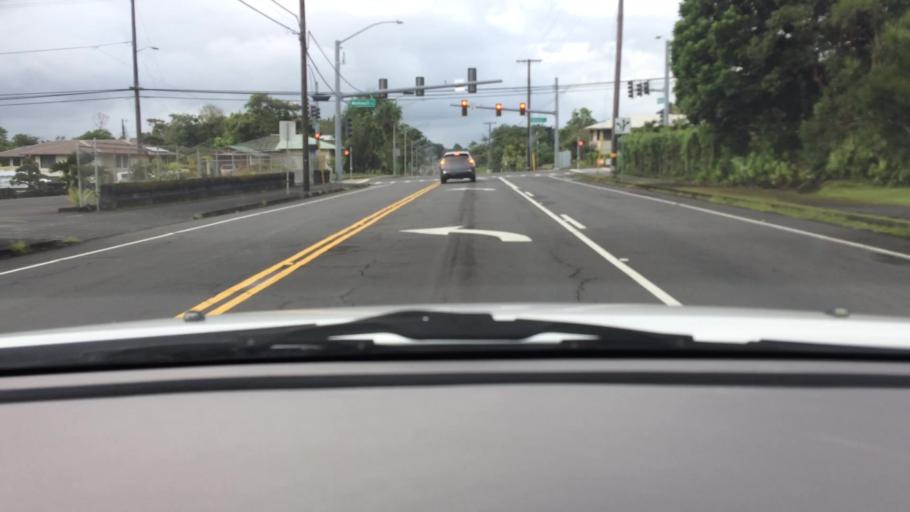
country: US
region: Hawaii
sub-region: Hawaii County
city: Hilo
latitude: 19.7108
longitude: -155.0836
